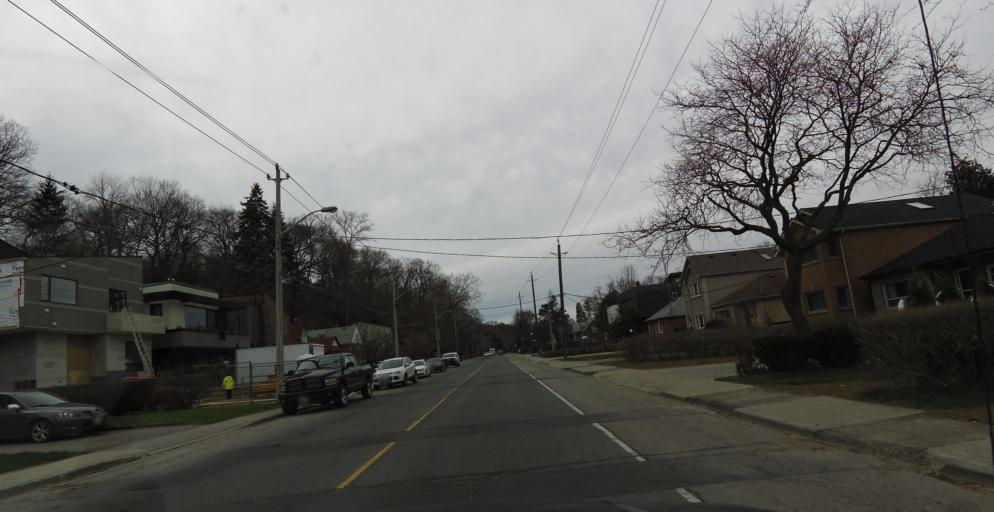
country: CA
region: Ontario
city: Toronto
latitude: 43.6403
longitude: -79.4779
